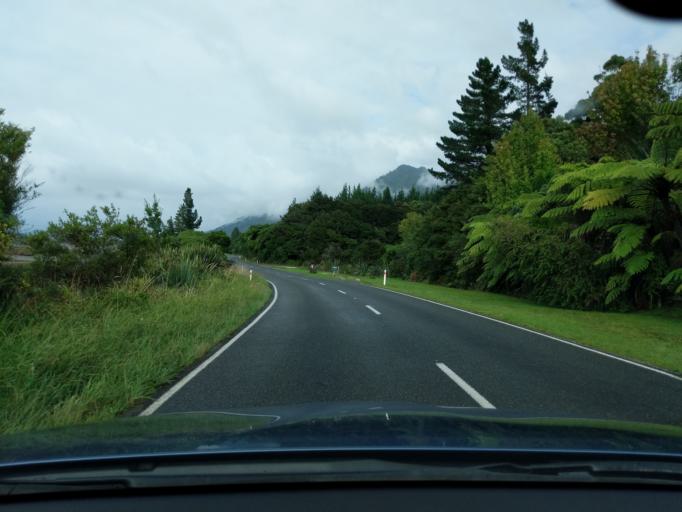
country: NZ
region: Tasman
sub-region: Tasman District
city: Takaka
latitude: -40.6398
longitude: 172.6669
